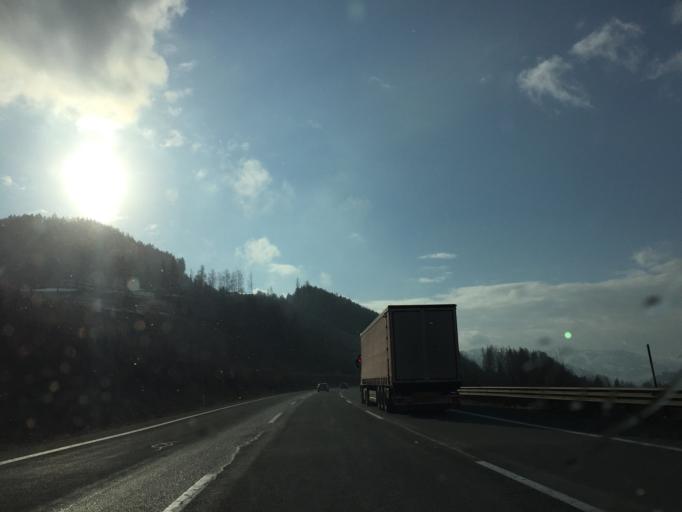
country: AT
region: Salzburg
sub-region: Politischer Bezirk Sankt Johann im Pongau
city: Pfarrwerfen
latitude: 47.4532
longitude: 13.2163
